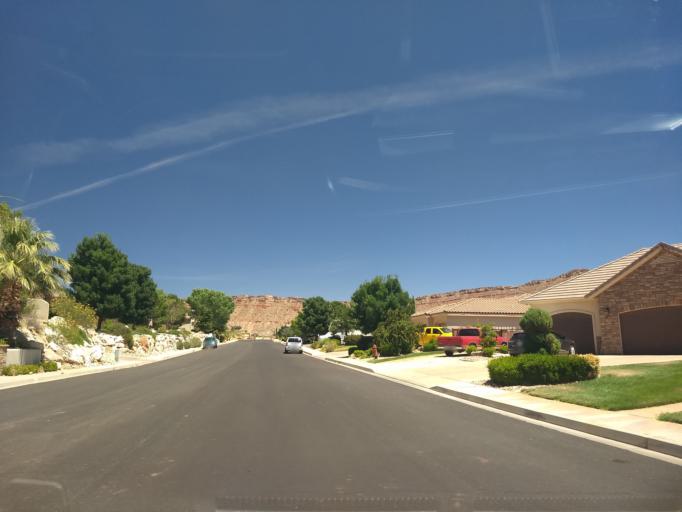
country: US
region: Utah
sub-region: Washington County
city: Washington
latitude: 37.0877
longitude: -113.4864
